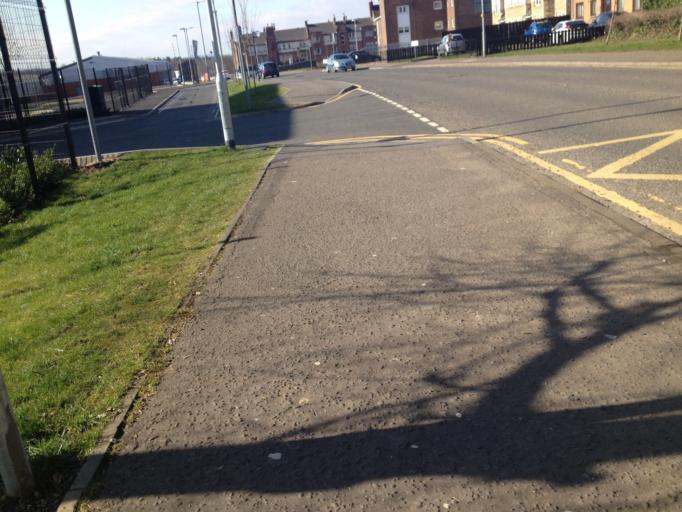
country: GB
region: Scotland
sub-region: South Lanarkshire
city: Hamilton
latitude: 55.7702
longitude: -4.0357
